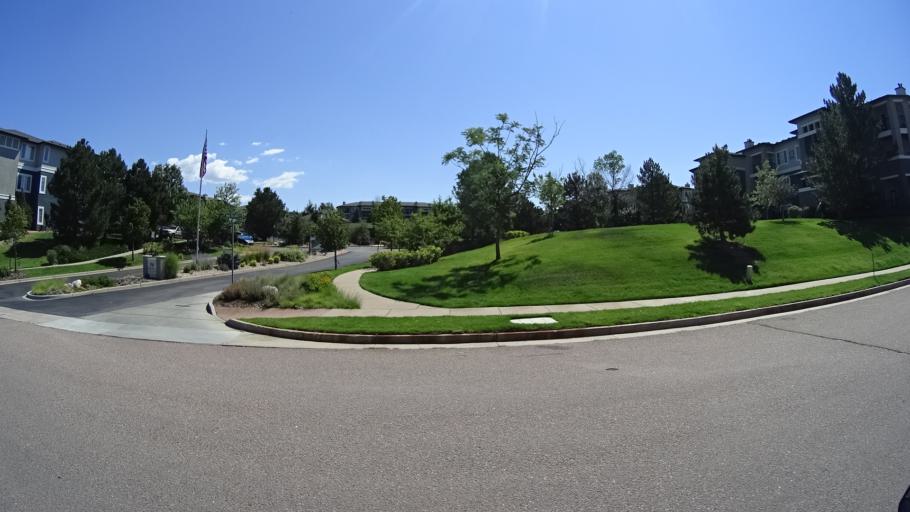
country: US
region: Colorado
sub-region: El Paso County
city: Air Force Academy
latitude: 38.9681
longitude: -104.7818
